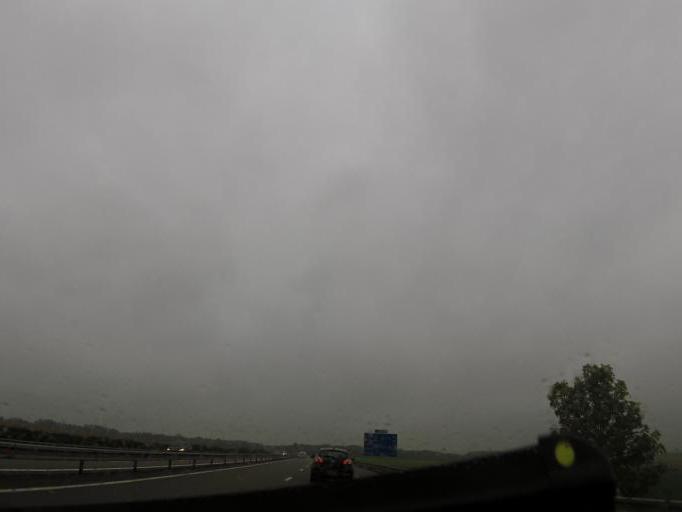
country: FR
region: Champagne-Ardenne
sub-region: Departement de la Marne
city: Saint-Memmie
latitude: 49.0360
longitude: 4.4221
